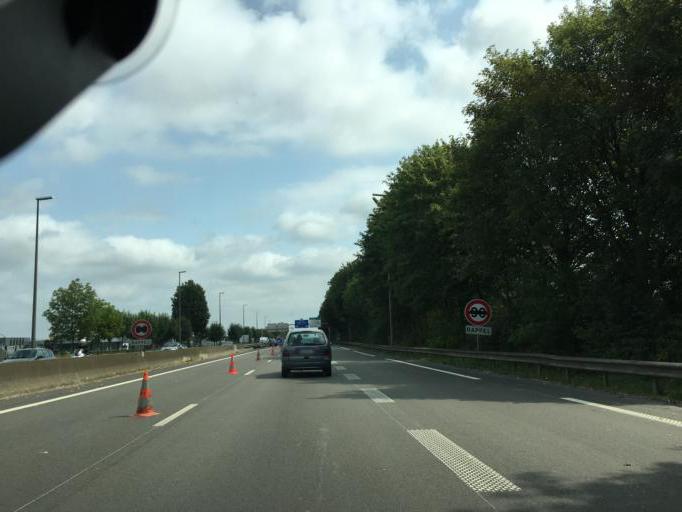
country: FR
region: Nord-Pas-de-Calais
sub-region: Departement du Pas-de-Calais
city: Lens
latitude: 50.4515
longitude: 2.8221
